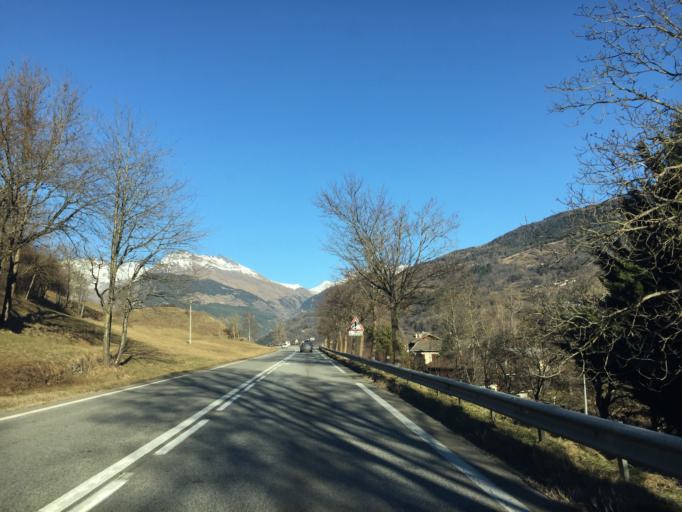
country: FR
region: Rhone-Alpes
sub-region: Departement de la Savoie
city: Bourg-Saint-Maurice
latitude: 45.5851
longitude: 6.7433
